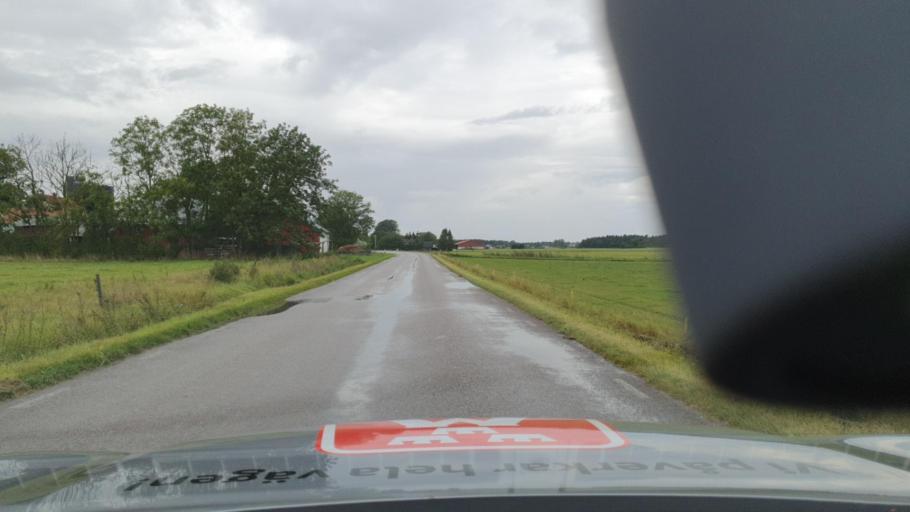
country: SE
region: Gotland
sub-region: Gotland
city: Slite
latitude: 57.5621
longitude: 18.5667
